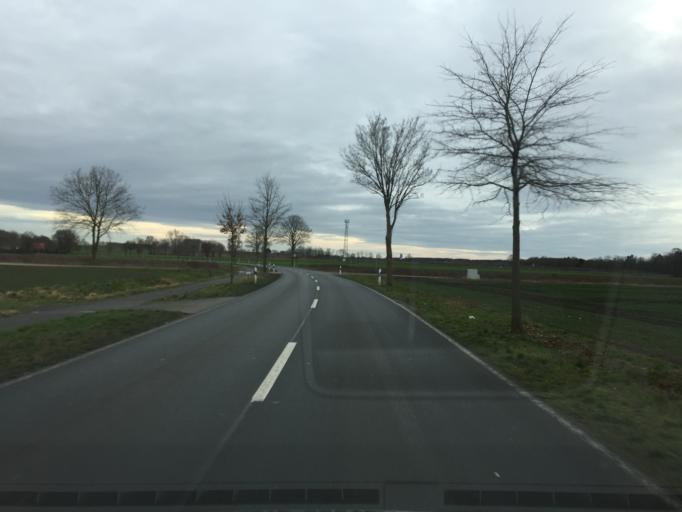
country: DE
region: Lower Saxony
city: Langwedel
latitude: 53.0098
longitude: 9.1704
